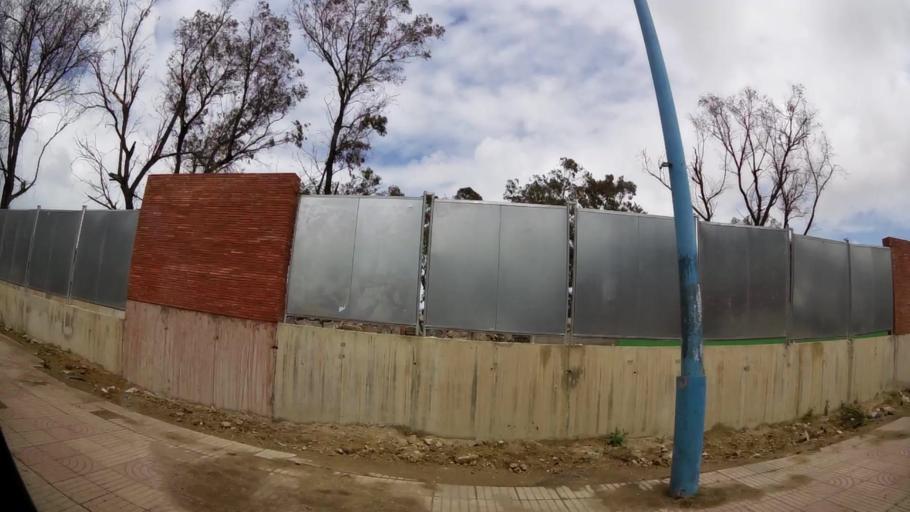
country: MA
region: Grand Casablanca
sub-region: Mediouna
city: Tit Mellil
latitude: 33.6040
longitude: -7.5327
